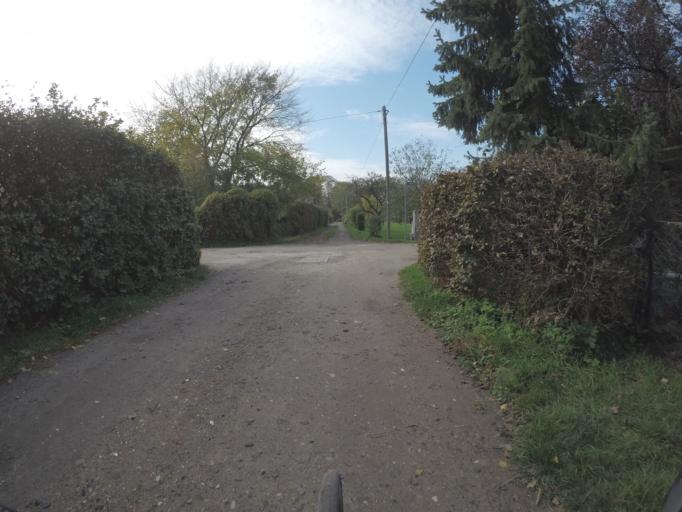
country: DE
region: Brandenburg
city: Leegebruch
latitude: 52.7472
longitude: 13.2008
